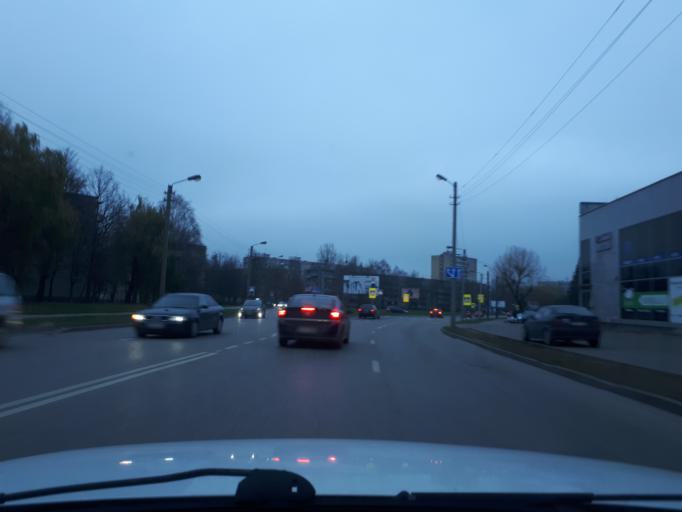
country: LT
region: Kauno apskritis
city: Dainava (Kaunas)
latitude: 54.9161
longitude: 23.9548
